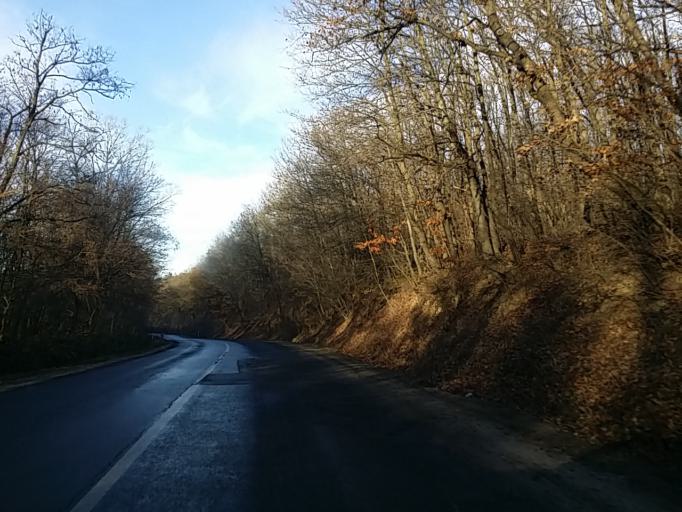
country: HU
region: Pest
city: Telki
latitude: 47.5365
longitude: 18.8549
